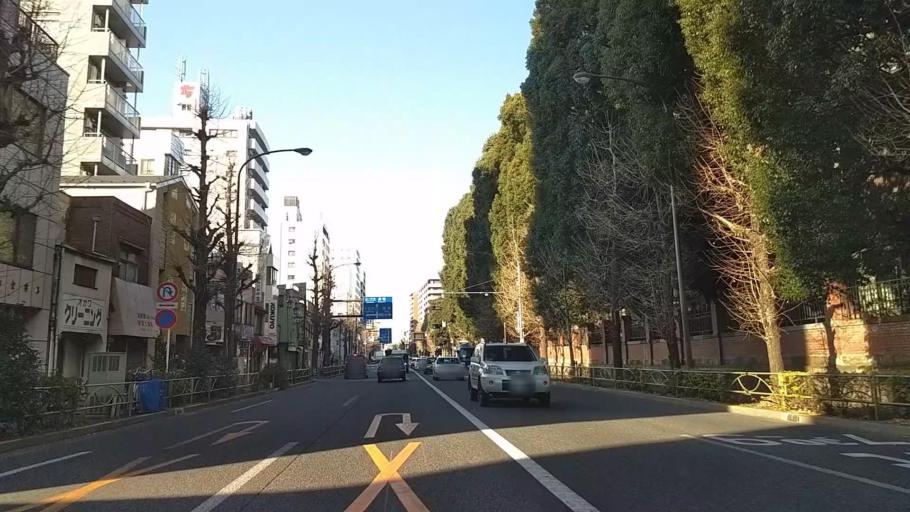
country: JP
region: Tokyo
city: Tokyo
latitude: 35.7143
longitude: 139.7591
